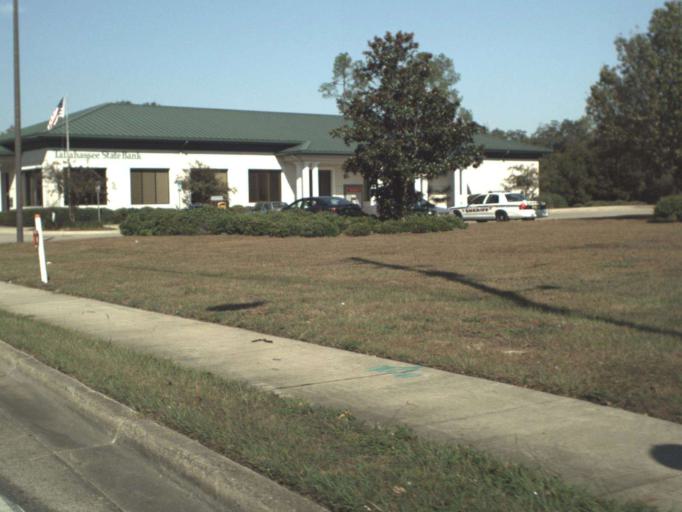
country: US
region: Florida
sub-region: Leon County
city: Tallahassee
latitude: 30.4533
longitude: -84.3384
